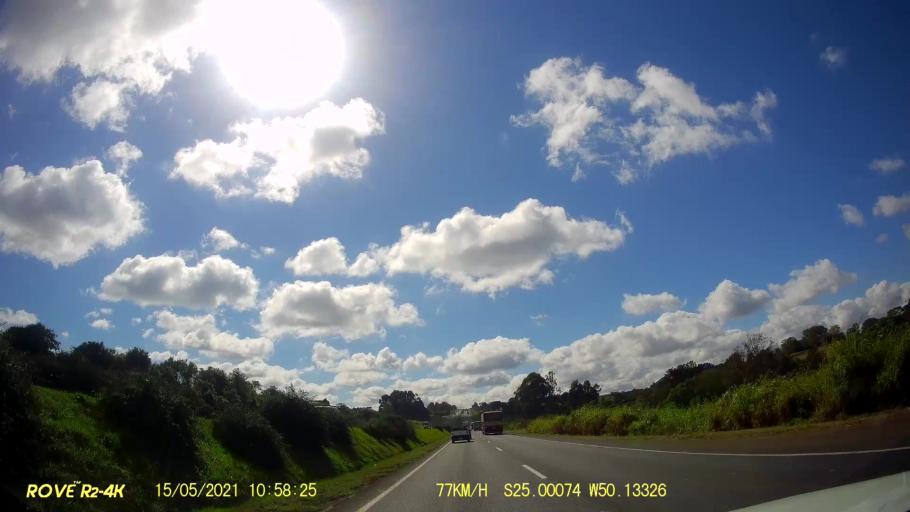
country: BR
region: Parana
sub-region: Carambei
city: Carambei
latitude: -25.0009
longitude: -50.1334
